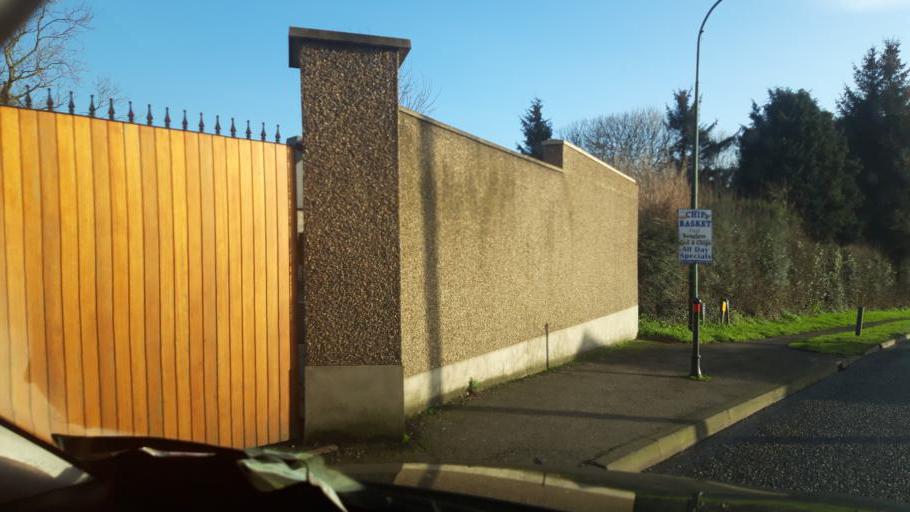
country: GB
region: Northern Ireland
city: Maghera
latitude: 54.8116
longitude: -6.7051
